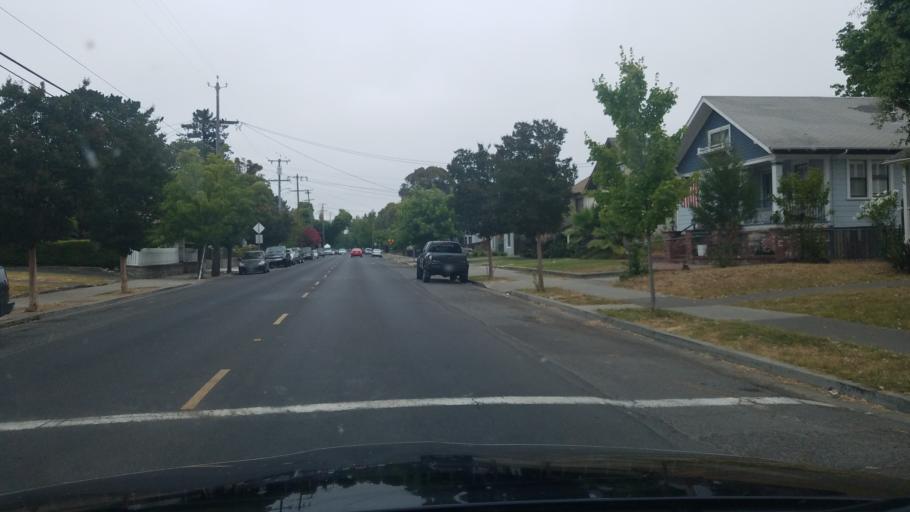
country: US
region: California
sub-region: Napa County
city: Napa
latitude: 38.2889
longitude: -122.2866
